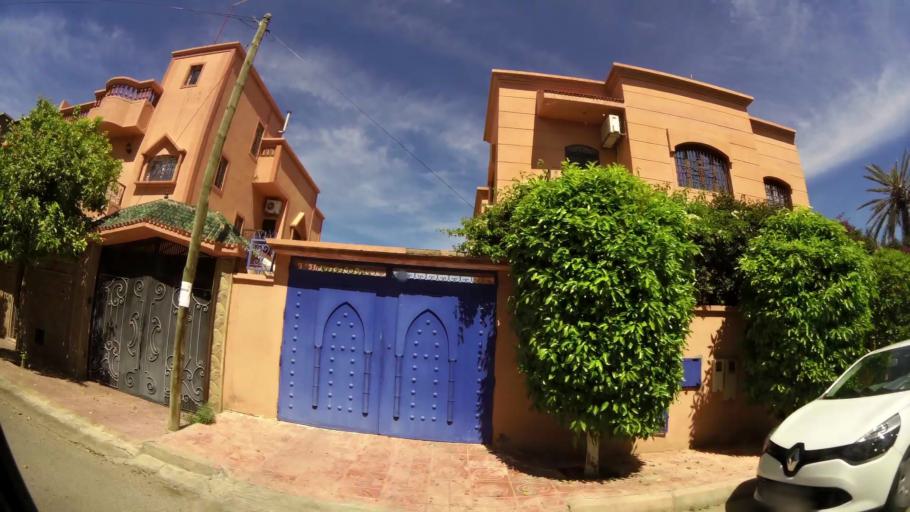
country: MA
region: Marrakech-Tensift-Al Haouz
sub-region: Marrakech
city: Marrakesh
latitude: 31.6659
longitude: -7.9937
